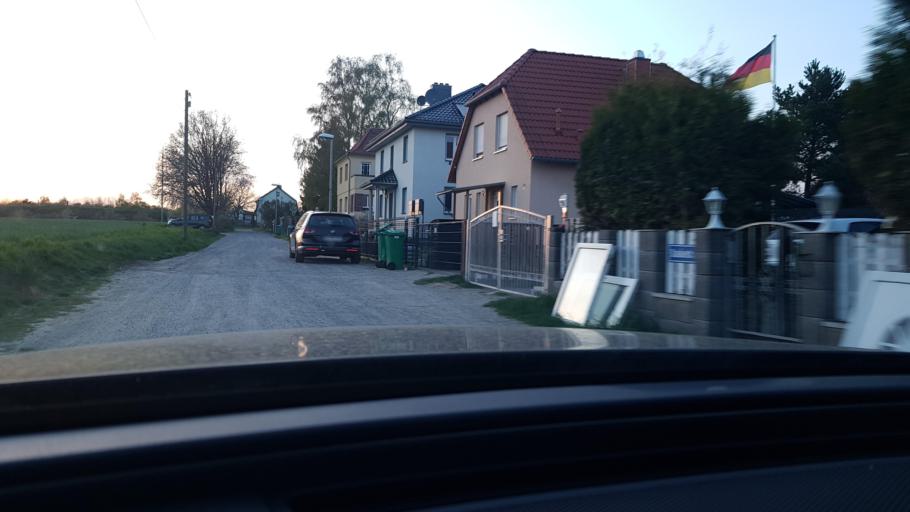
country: DE
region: Berlin
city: Lichtenrade
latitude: 52.3513
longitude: 13.4239
